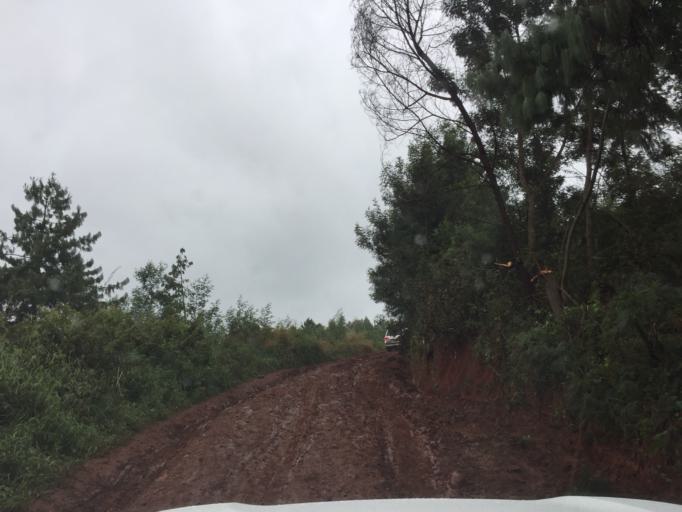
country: TZ
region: Iringa
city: Iringa
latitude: -8.1216
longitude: 35.8994
